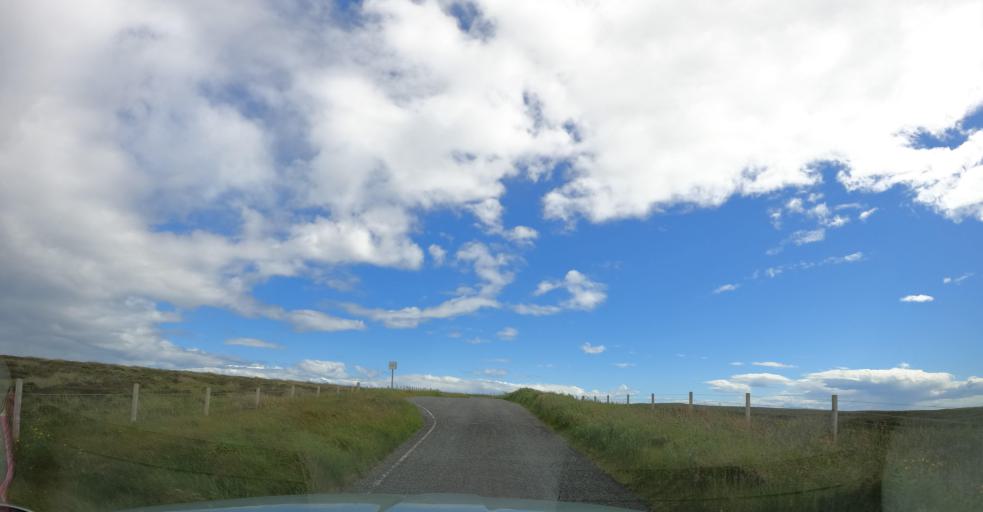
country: GB
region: Scotland
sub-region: Eilean Siar
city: Stornoway
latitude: 58.2052
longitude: -6.2468
